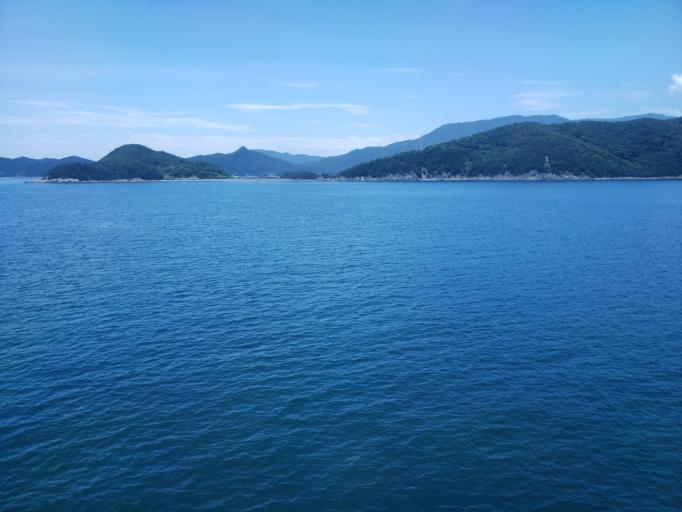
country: JP
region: Kagawa
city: Tonosho
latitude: 34.4377
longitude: 134.2957
